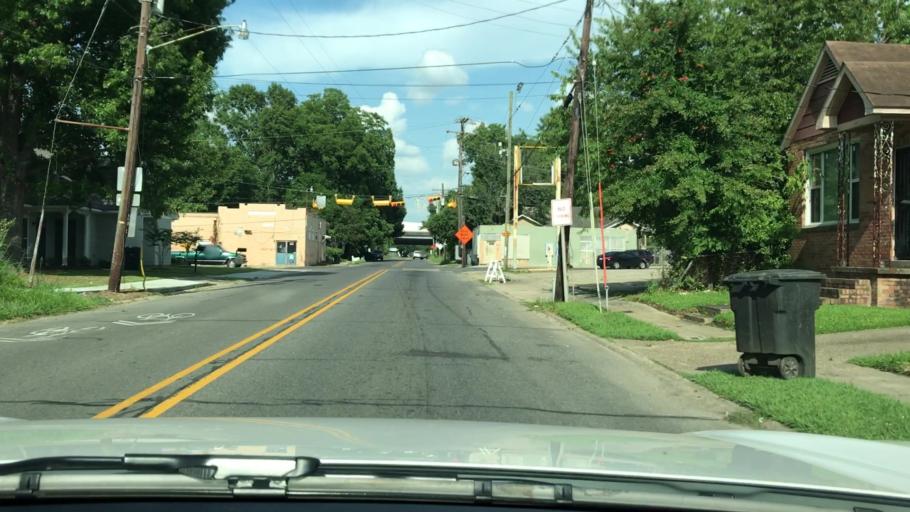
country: US
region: Louisiana
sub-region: East Baton Rouge Parish
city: Baton Rouge
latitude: 30.4363
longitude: -91.1808
